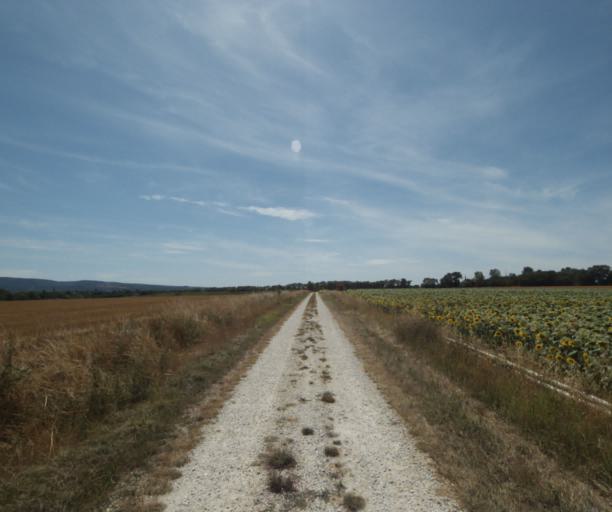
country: FR
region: Midi-Pyrenees
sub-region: Departement de la Haute-Garonne
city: Revel
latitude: 43.5052
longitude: 2.0182
